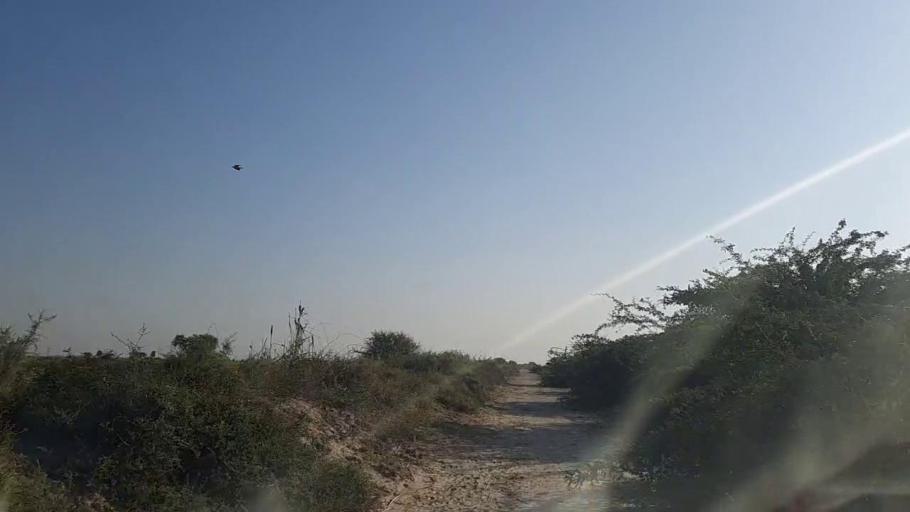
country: PK
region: Sindh
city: Jati
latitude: 24.3940
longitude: 68.2302
